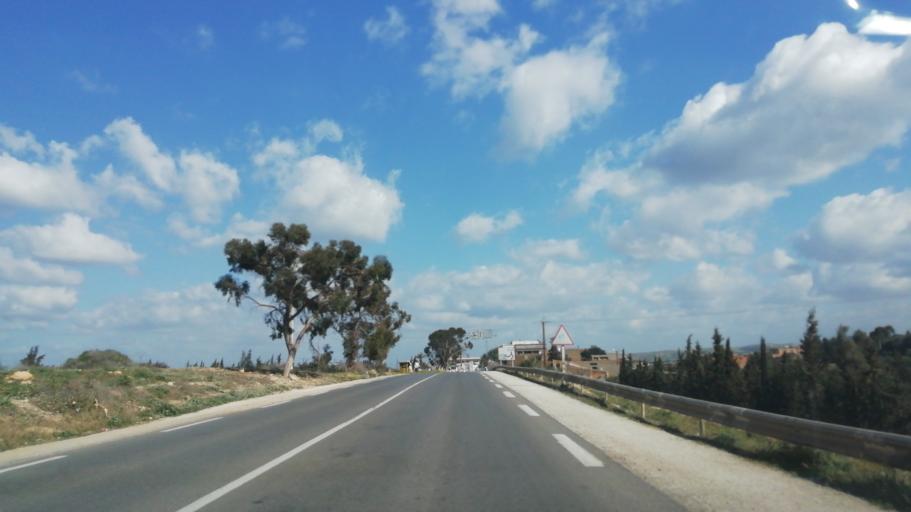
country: DZ
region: Relizane
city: Relizane
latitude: 35.7202
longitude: 0.3195
